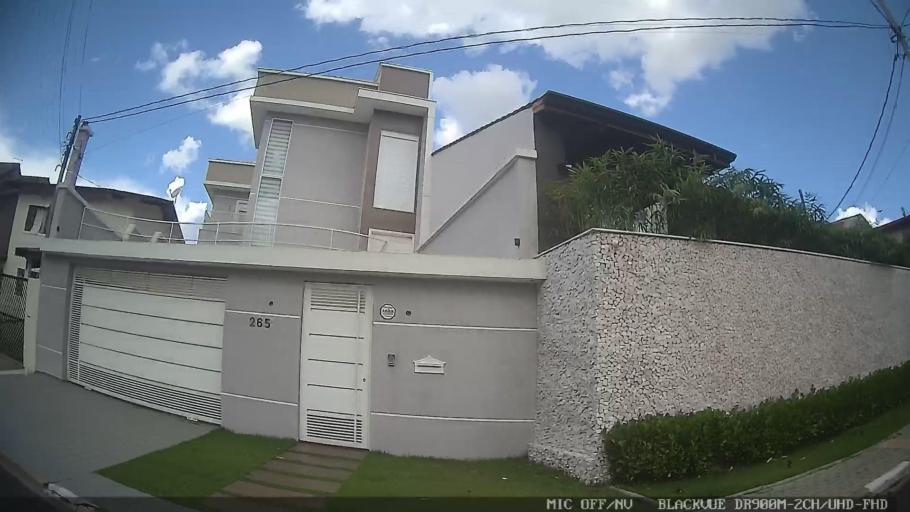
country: BR
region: Sao Paulo
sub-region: Atibaia
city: Atibaia
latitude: -23.1324
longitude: -46.5564
